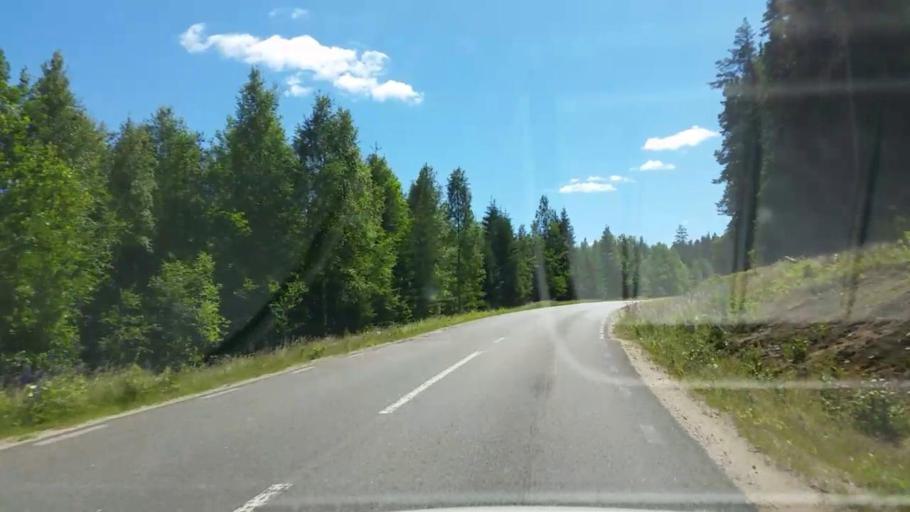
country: SE
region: Gaevleborg
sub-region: Ljusdals Kommun
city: Farila
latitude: 61.6914
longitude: 15.6503
